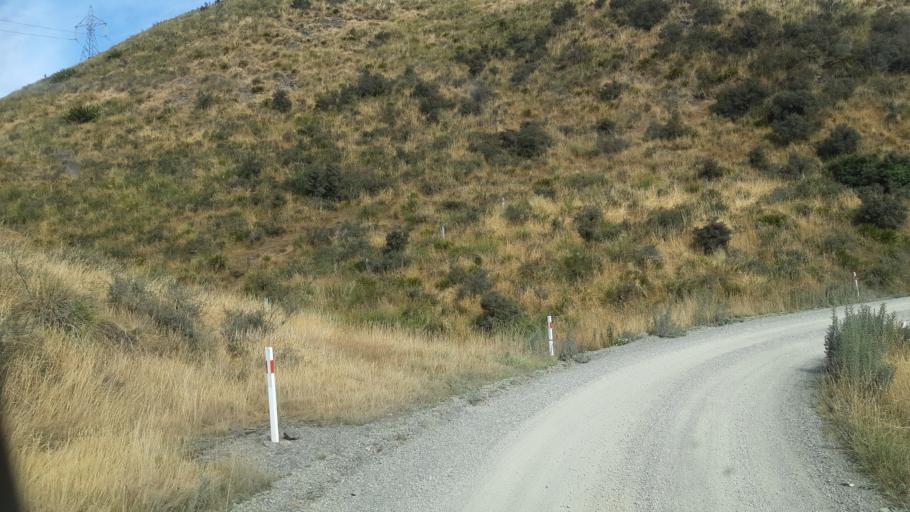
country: NZ
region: Canterbury
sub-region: Timaru District
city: Pleasant Point
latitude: -44.1940
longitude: 170.6106
